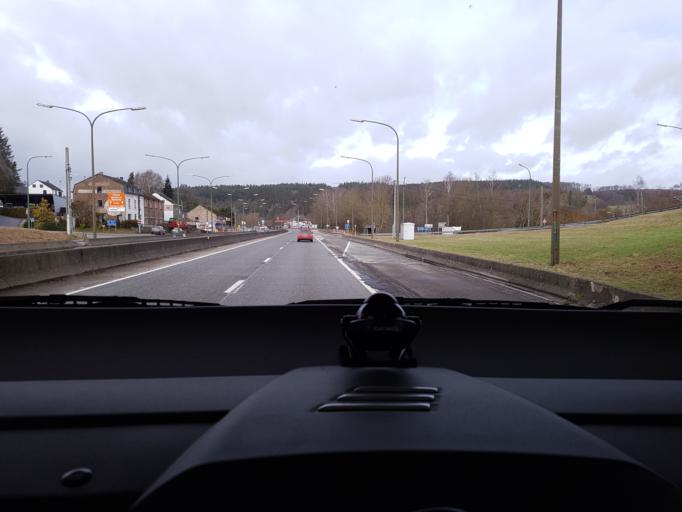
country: BE
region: Wallonia
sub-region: Province du Luxembourg
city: Nassogne
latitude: 50.1605
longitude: 5.4088
